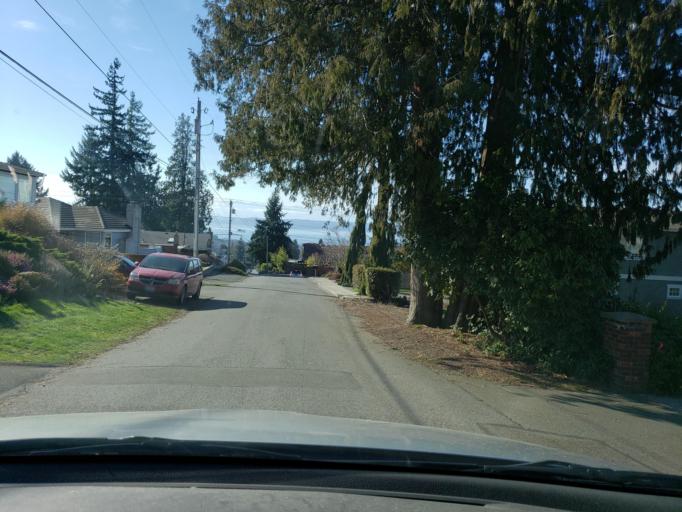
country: US
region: Washington
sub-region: Snohomish County
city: Edmonds
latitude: 47.8065
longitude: -122.3658
